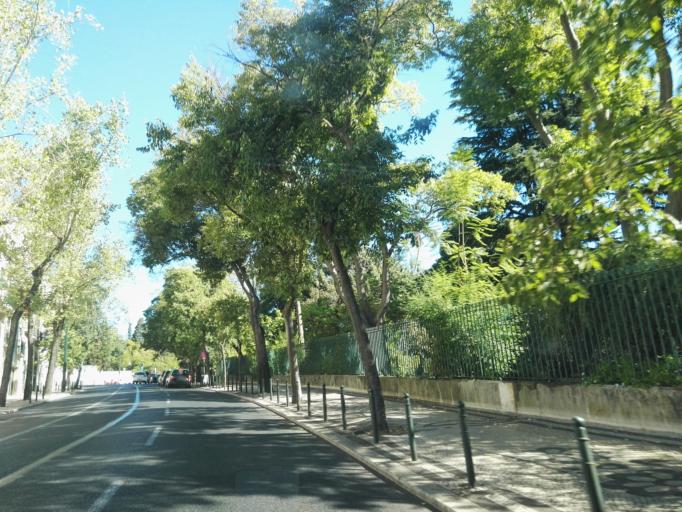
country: PT
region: Lisbon
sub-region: Lisbon
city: Lisbon
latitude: 38.7146
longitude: -9.1606
